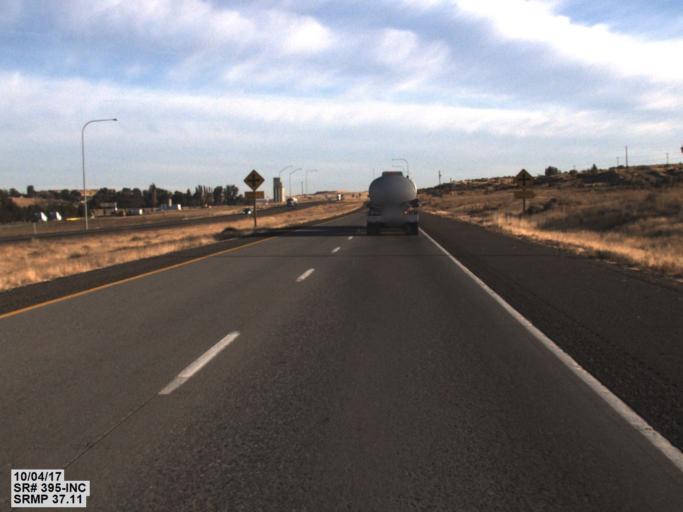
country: US
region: Washington
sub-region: Franklin County
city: Basin City
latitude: 46.4447
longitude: -119.0191
